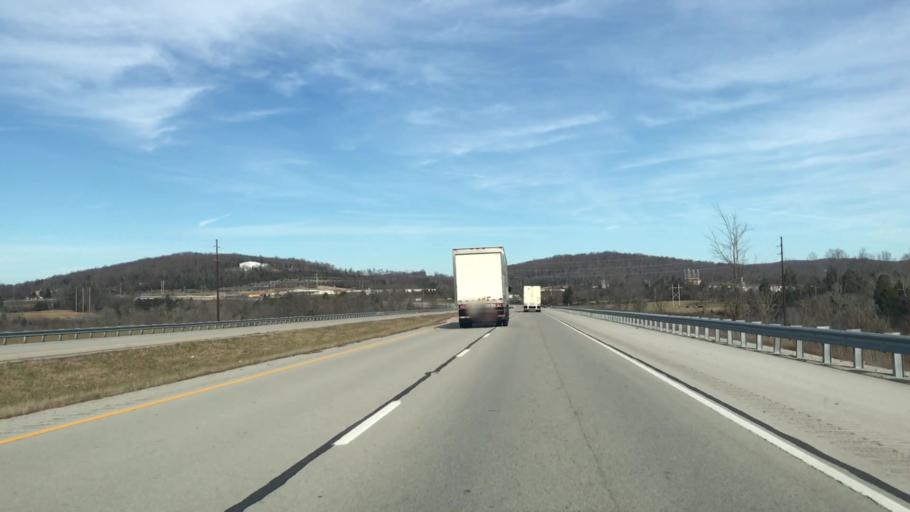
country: US
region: Kentucky
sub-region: Pulaski County
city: Somerset
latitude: 37.0401
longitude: -84.5869
